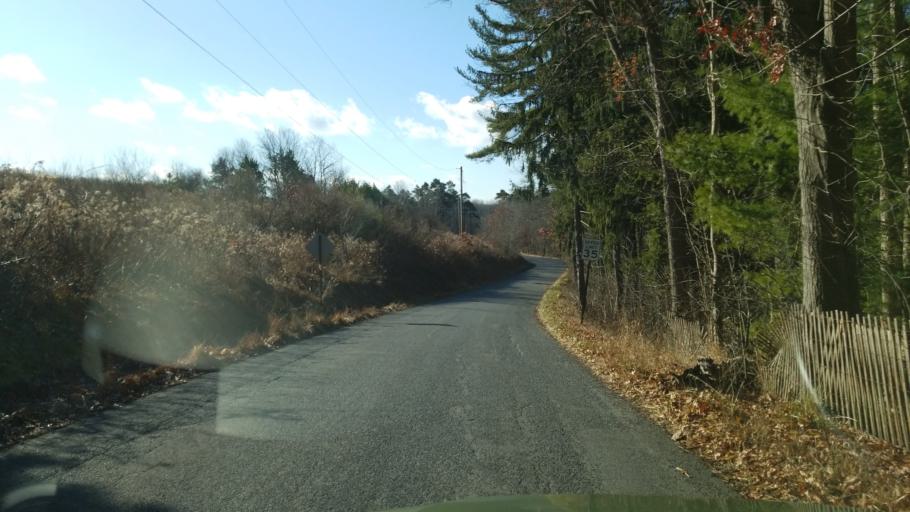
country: US
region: Pennsylvania
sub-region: Clearfield County
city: Clearfield
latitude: 41.0066
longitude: -78.4191
